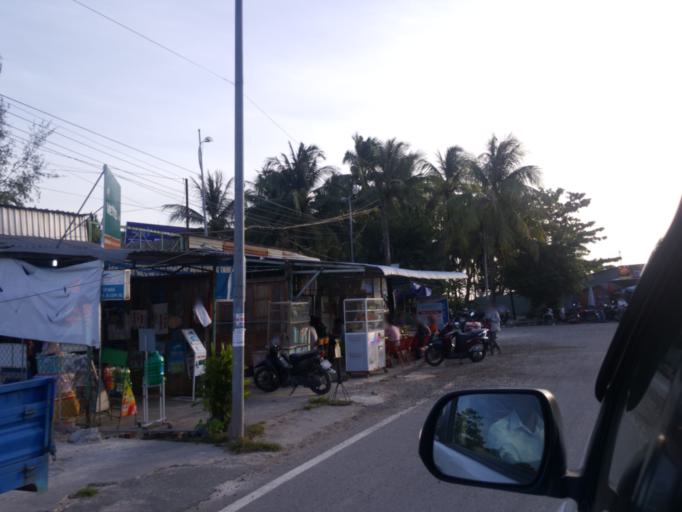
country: VN
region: Kien Giang
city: Duong GJong
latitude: 10.1494
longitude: 104.0370
